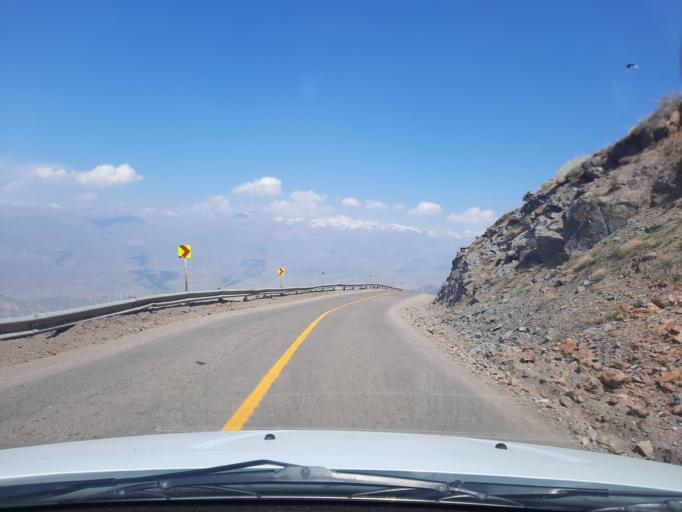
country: IR
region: Qazvin
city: Qazvin
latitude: 36.3957
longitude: 50.2109
